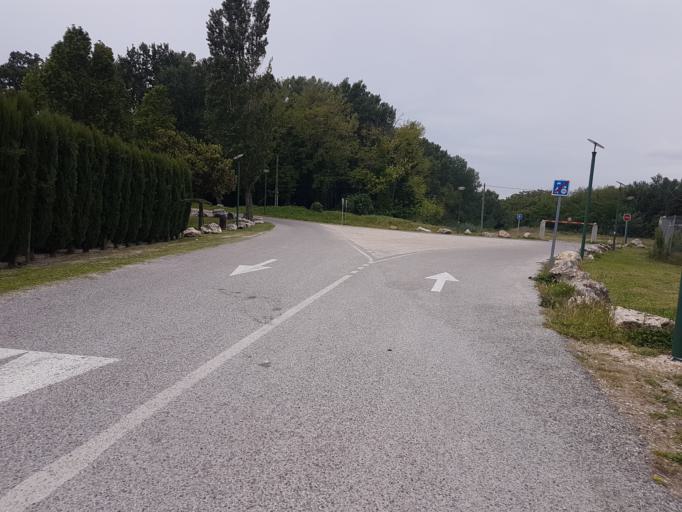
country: FR
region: Languedoc-Roussillon
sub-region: Departement du Gard
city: Roquemaure
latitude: 44.0543
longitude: 4.7776
